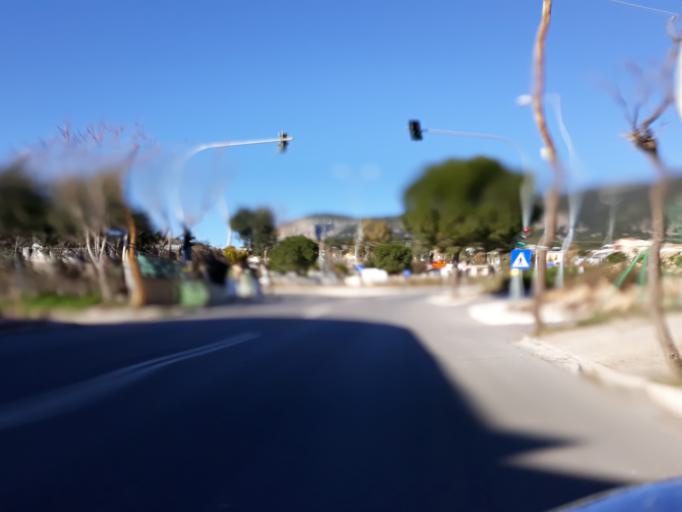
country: GR
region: Attica
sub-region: Nomarchia Dytikis Attikis
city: Ano Liosia
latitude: 38.0936
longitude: 23.6879
